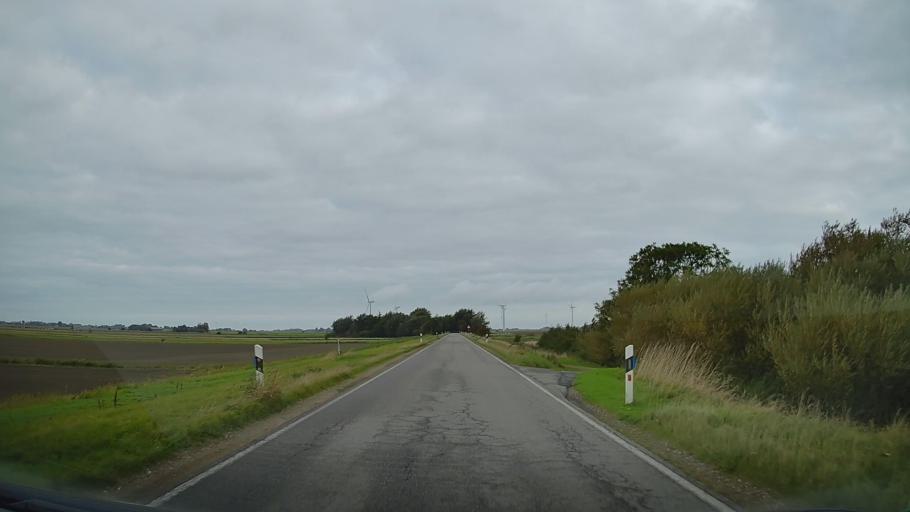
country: DE
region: Schleswig-Holstein
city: Galmsbull
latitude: 54.7822
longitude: 8.7327
